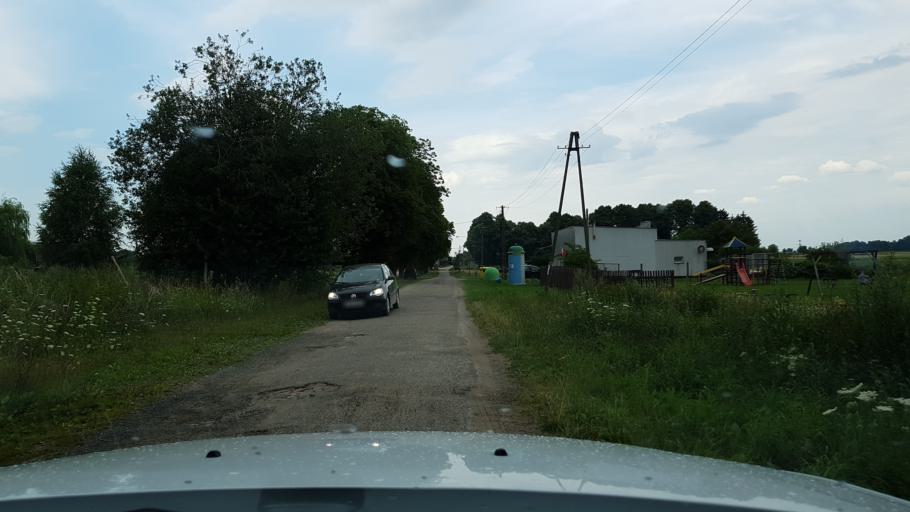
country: PL
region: West Pomeranian Voivodeship
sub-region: Powiat walecki
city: Walcz
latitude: 53.3511
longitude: 16.3589
